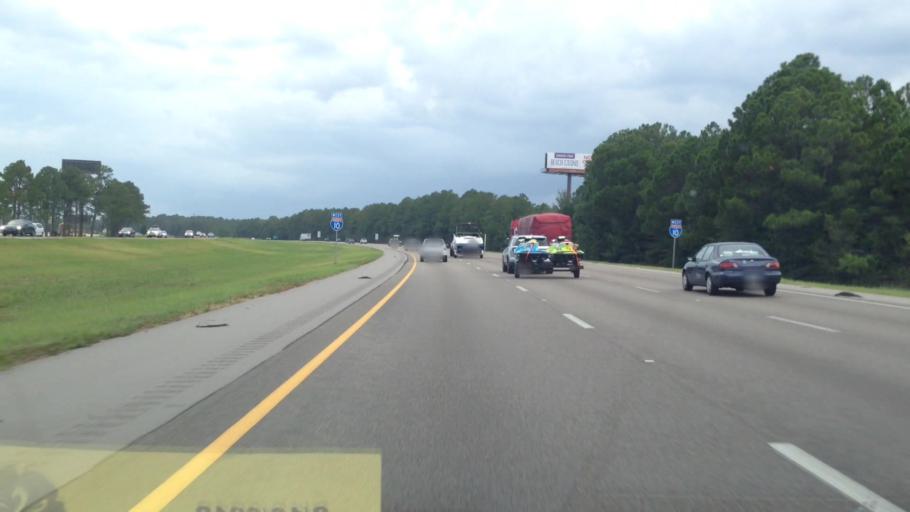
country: US
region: Mississippi
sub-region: Harrison County
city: D'Iberville
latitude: 30.4609
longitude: -88.9781
